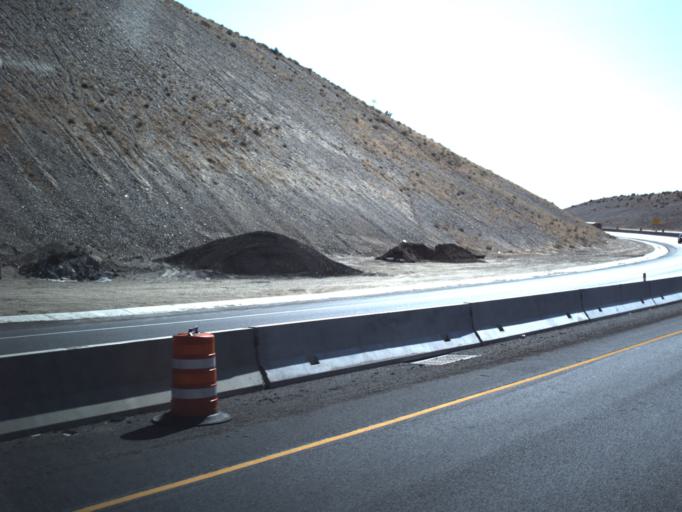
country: US
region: Utah
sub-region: Box Elder County
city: Brigham City
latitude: 41.4993
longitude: -111.9928
